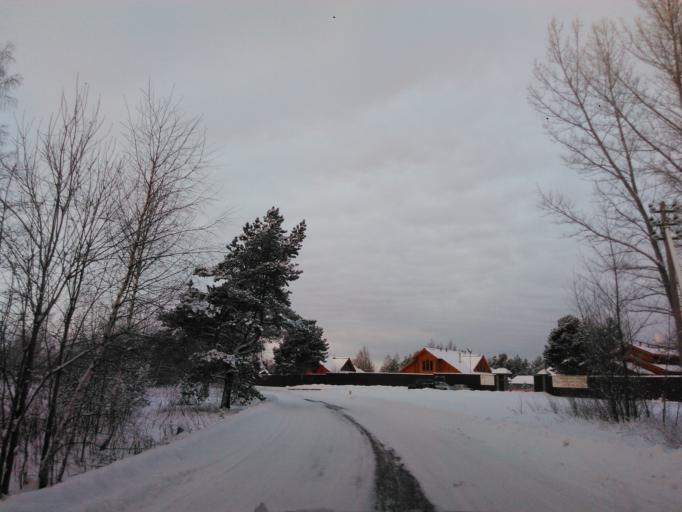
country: RU
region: Tverskaya
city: Konakovo
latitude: 56.6479
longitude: 36.6441
